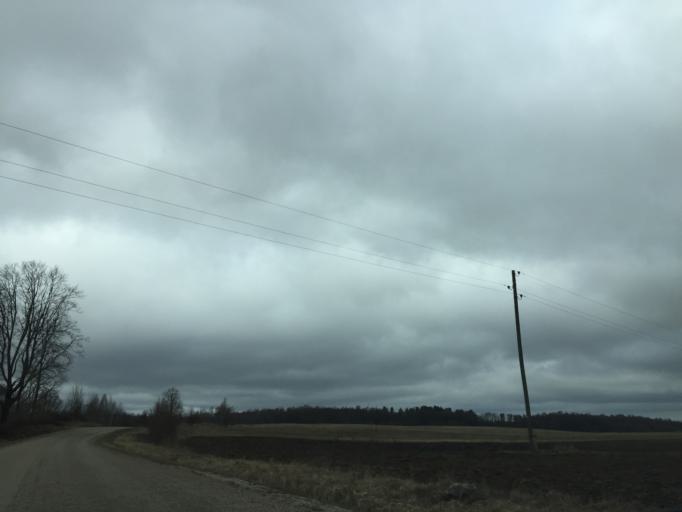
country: LV
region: Ilukste
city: Ilukste
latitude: 56.0123
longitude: 26.2682
